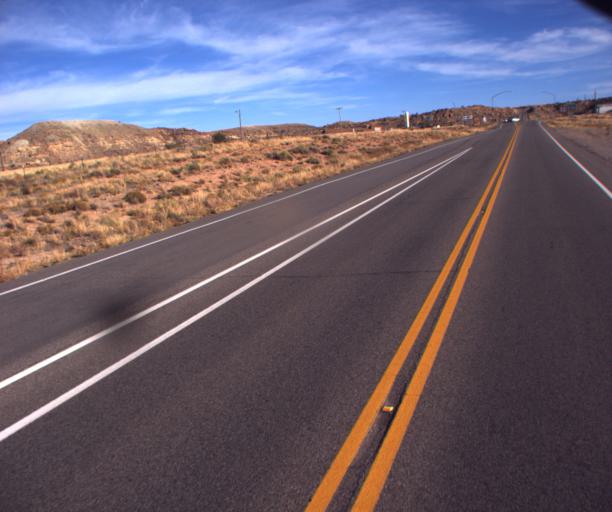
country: US
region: New Mexico
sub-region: San Juan County
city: Shiprock
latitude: 36.9221
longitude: -109.0895
